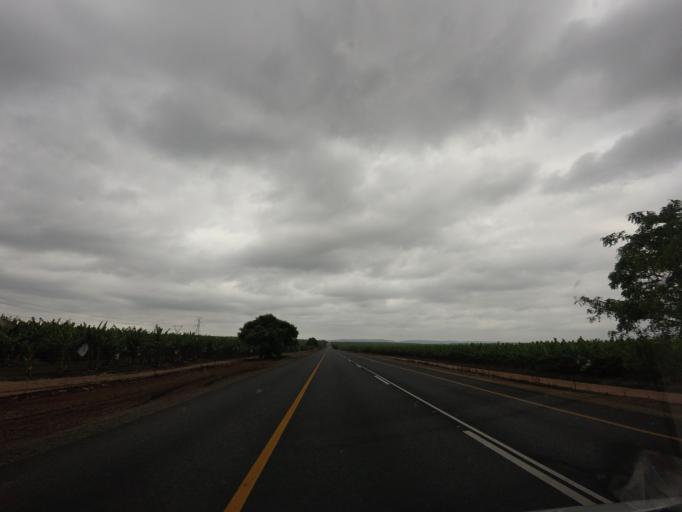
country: ZA
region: Mpumalanga
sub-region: Ehlanzeni District
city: Komatipoort
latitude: -25.4360
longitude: 31.8280
